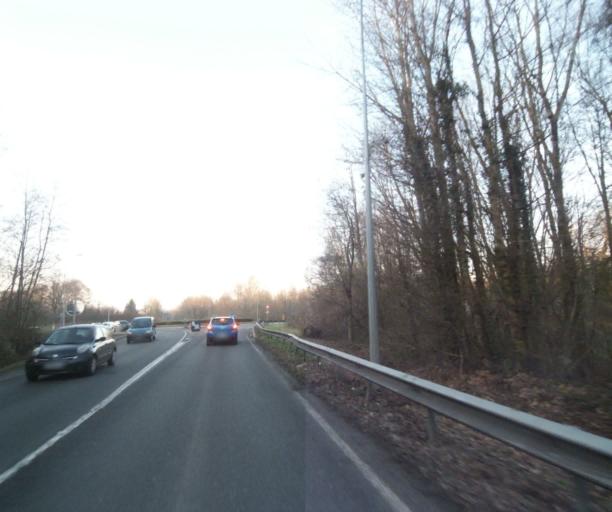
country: FR
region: Lorraine
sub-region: Departement de la Meuse
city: Ancerville
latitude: 48.6221
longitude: 4.9940
